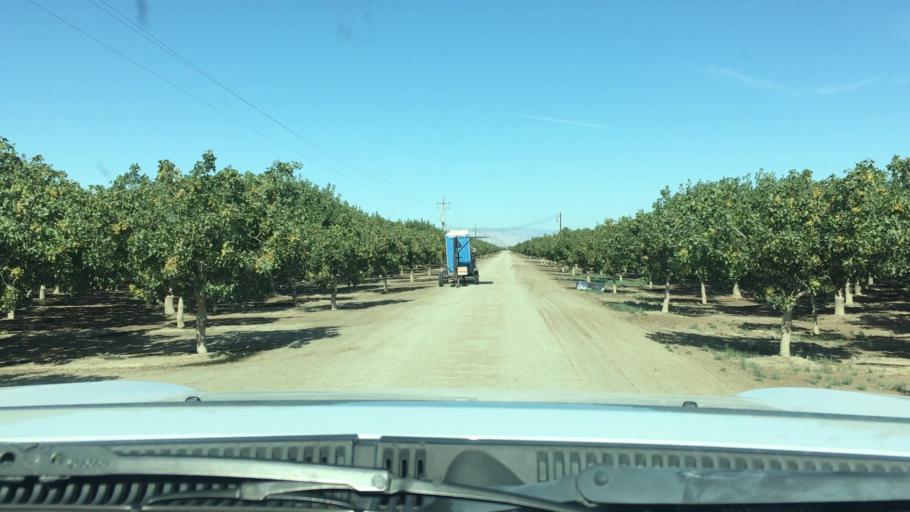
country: US
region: California
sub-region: Kern County
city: Buttonwillow
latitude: 35.3694
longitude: -119.3911
